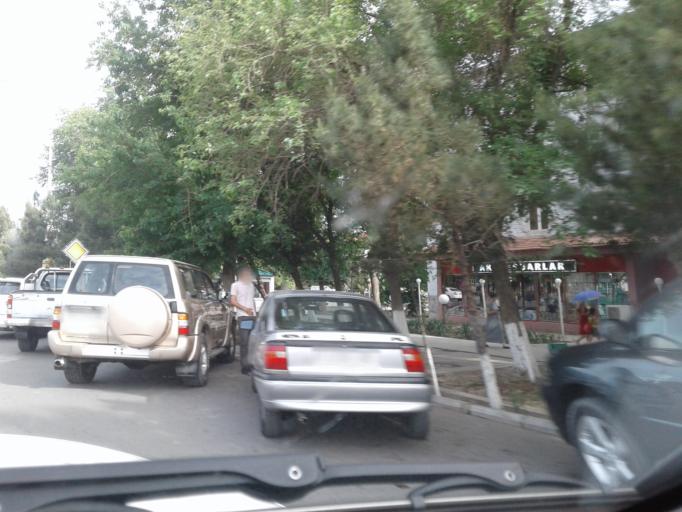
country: TM
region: Mary
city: Mary
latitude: 37.5927
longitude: 61.8427
